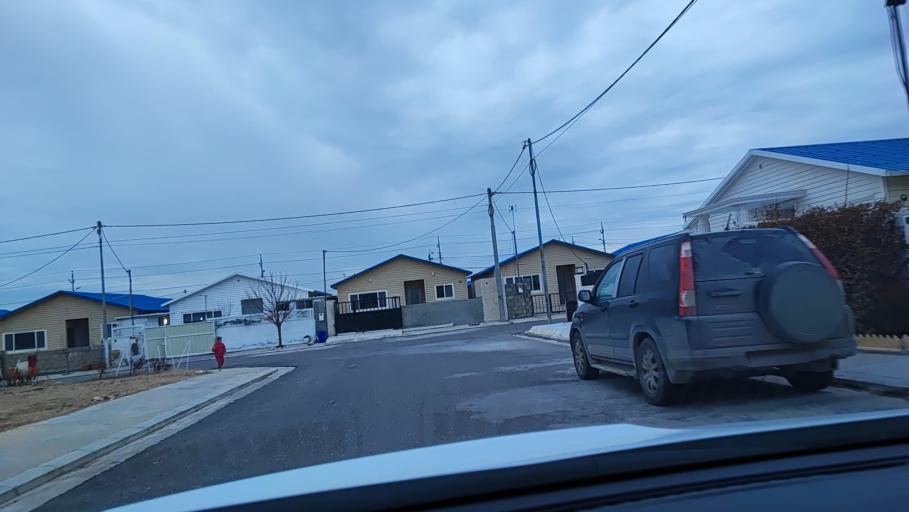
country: IQ
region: Arbil
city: Erbil
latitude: 36.2868
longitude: 44.0796
